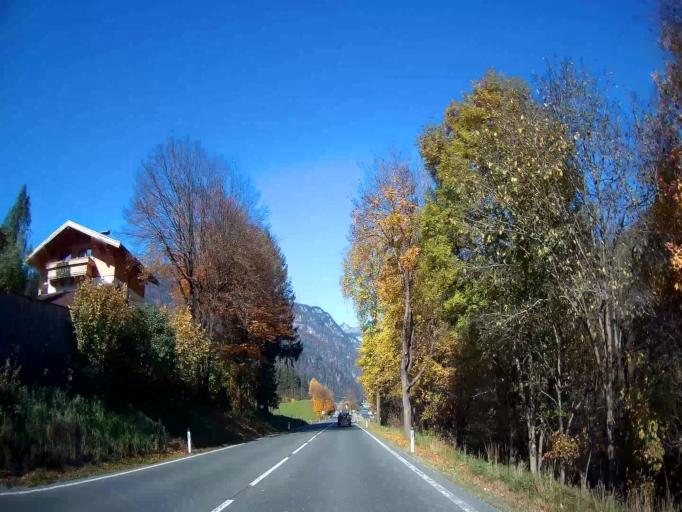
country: AT
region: Salzburg
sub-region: Politischer Bezirk Zell am See
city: Saalfelden am Steinernen Meer
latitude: 47.4474
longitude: 12.8361
